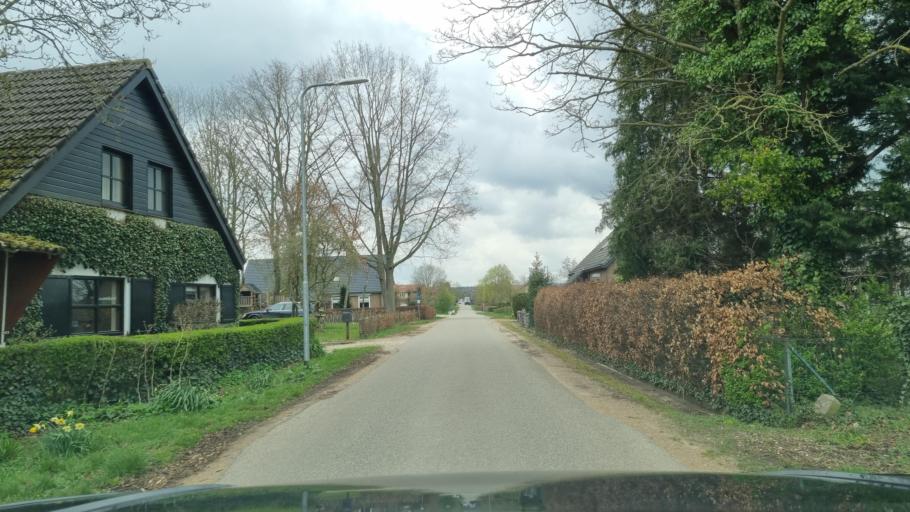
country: NL
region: Gelderland
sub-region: Gemeente Groesbeek
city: Bredeweg
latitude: 51.7561
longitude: 5.9585
